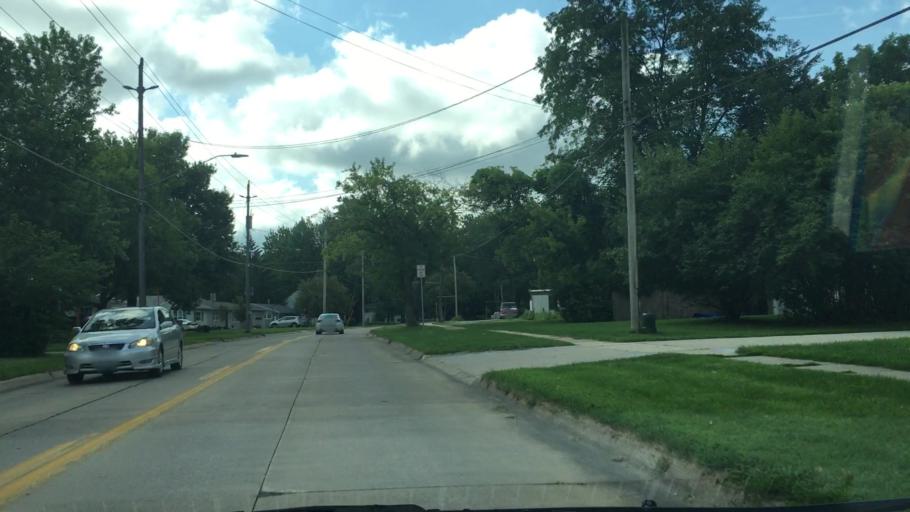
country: US
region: Iowa
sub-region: Johnson County
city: Iowa City
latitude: 41.6833
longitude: -91.5221
